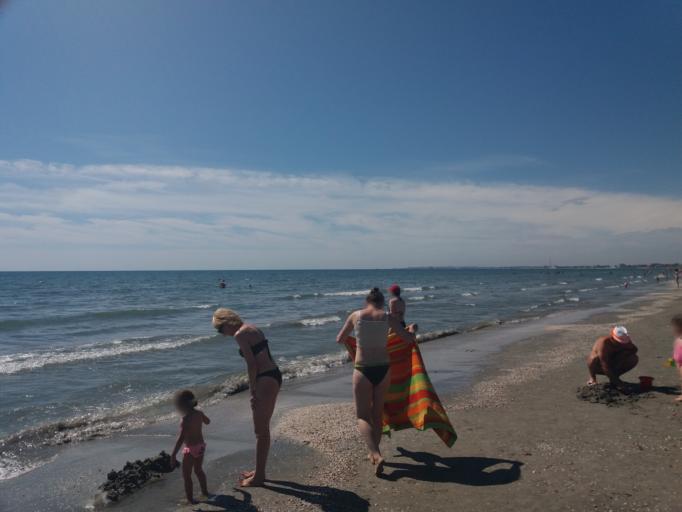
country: RO
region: Constanta
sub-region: Comuna Navodari
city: Navodari
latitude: 44.3191
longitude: 28.6359
